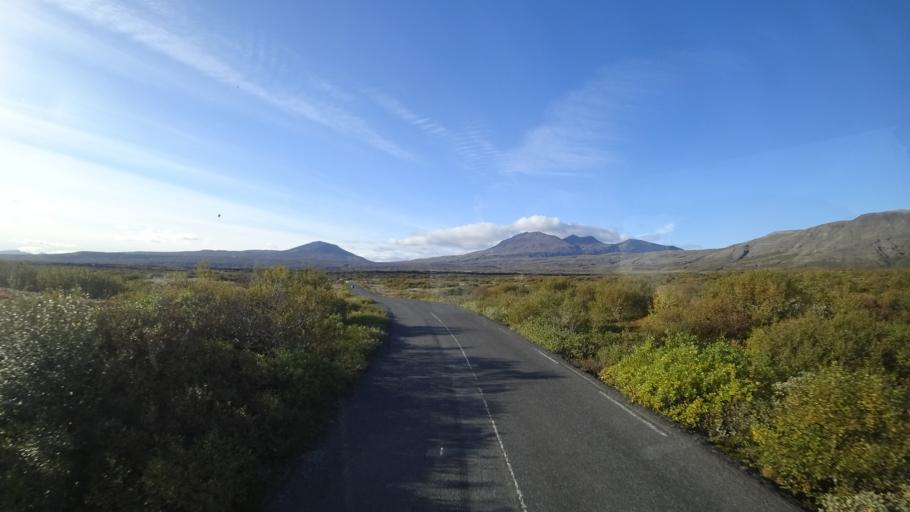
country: IS
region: South
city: Hveragerdi
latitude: 64.2773
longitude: -21.0758
